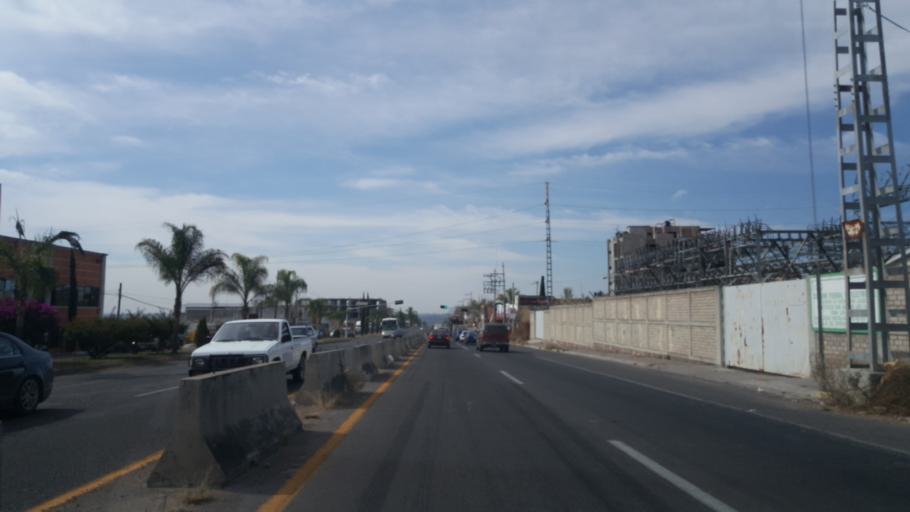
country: MX
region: Jalisco
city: San Juan de los Lagos
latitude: 21.2665
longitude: -102.3115
